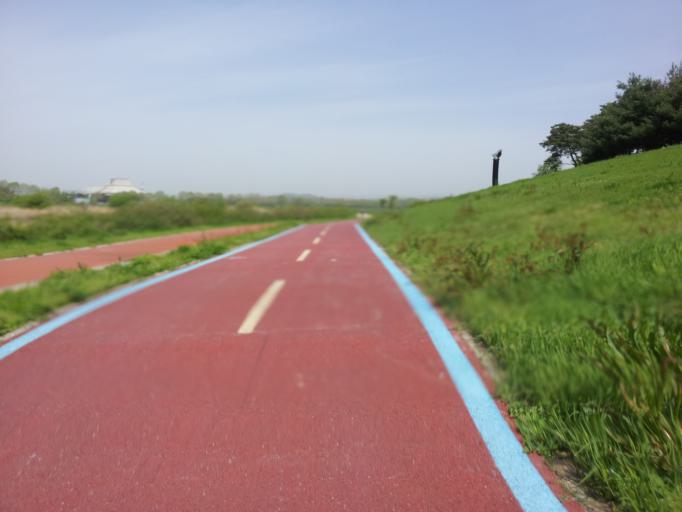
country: KR
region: Daejeon
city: Daejeon
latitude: 36.3632
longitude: 127.3987
